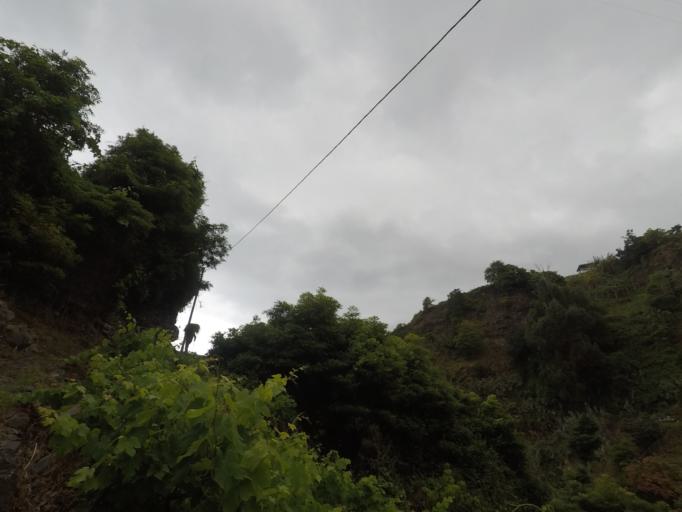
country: PT
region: Madeira
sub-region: Santana
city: Santana
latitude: 32.7582
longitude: -16.8289
